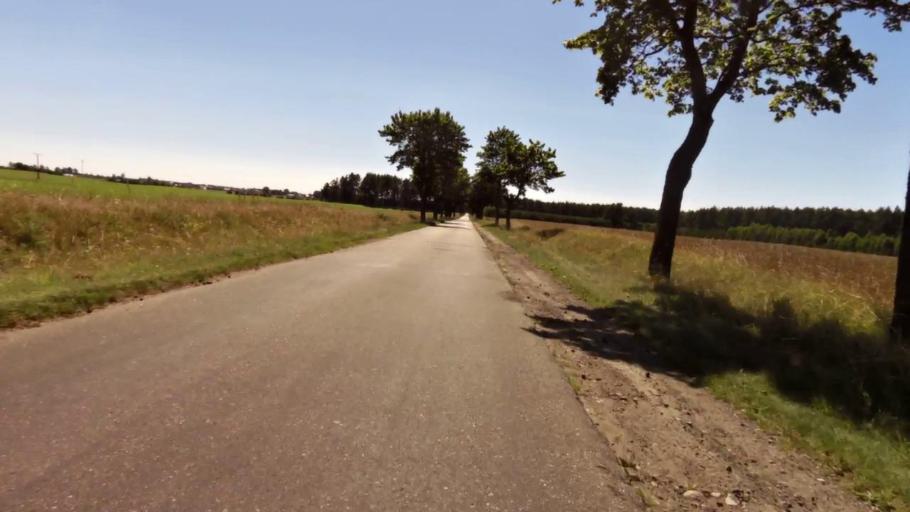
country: PL
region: West Pomeranian Voivodeship
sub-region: Powiat szczecinecki
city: Bialy Bor
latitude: 53.9162
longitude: 16.8386
